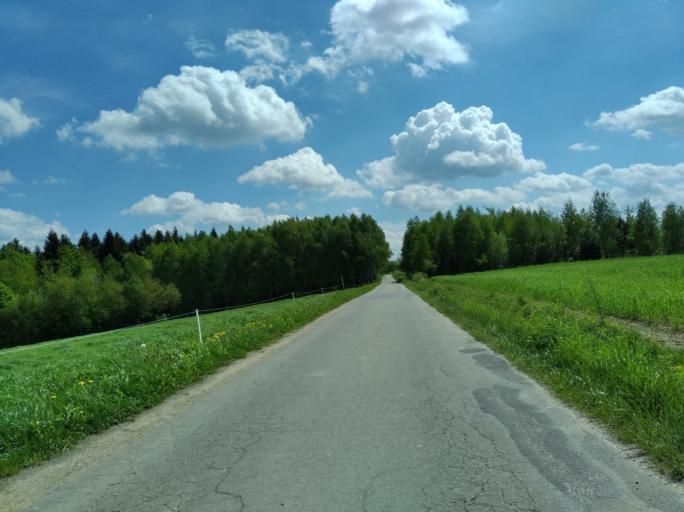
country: PL
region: Subcarpathian Voivodeship
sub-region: Powiat jasielski
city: Kolaczyce
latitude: 49.8431
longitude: 21.4471
